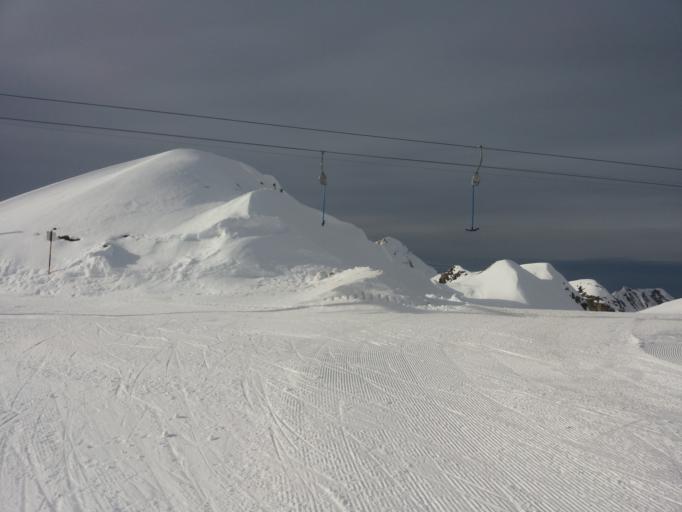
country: CH
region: Bern
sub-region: Interlaken-Oberhasli District
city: Meiringen
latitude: 46.7612
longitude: 8.2212
